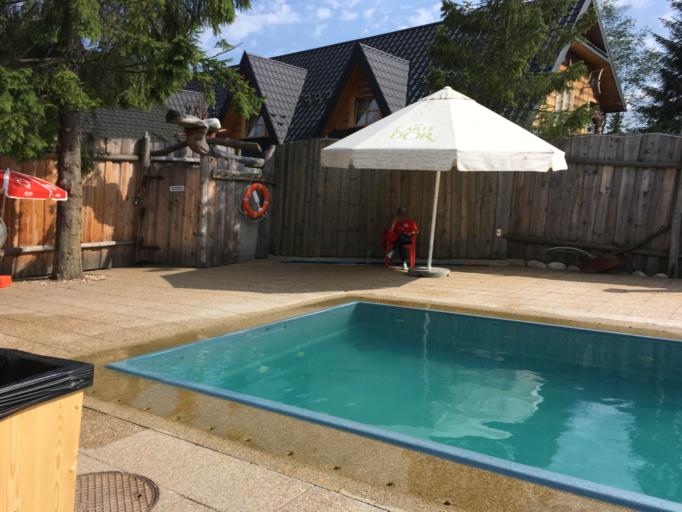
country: PL
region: Lesser Poland Voivodeship
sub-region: Powiat nowotarski
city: Szaflary
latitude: 49.3993
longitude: 20.0225
